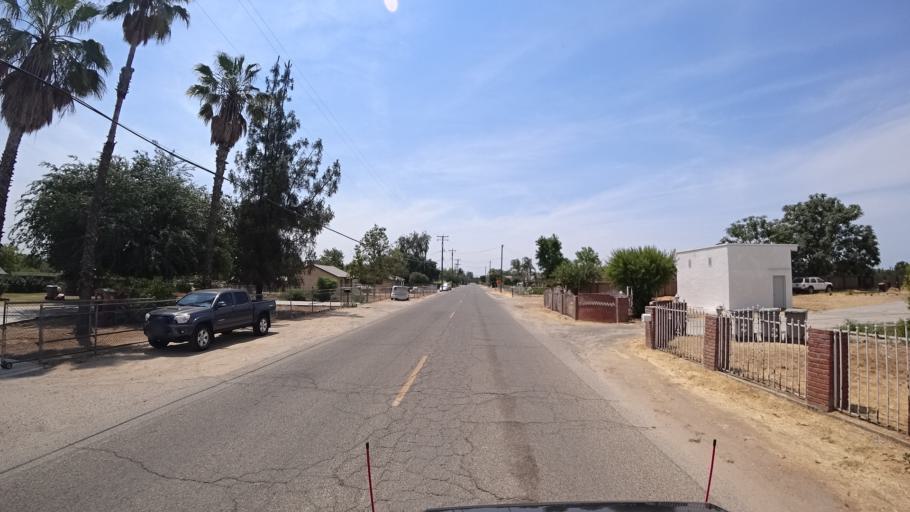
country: US
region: California
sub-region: Fresno County
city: West Park
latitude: 36.7595
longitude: -119.8533
